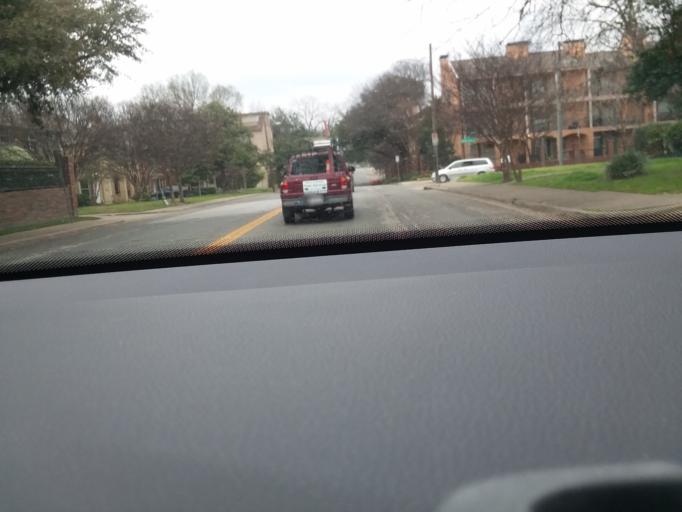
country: US
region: Texas
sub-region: Dallas County
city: Highland Park
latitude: 32.8162
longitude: -96.7557
